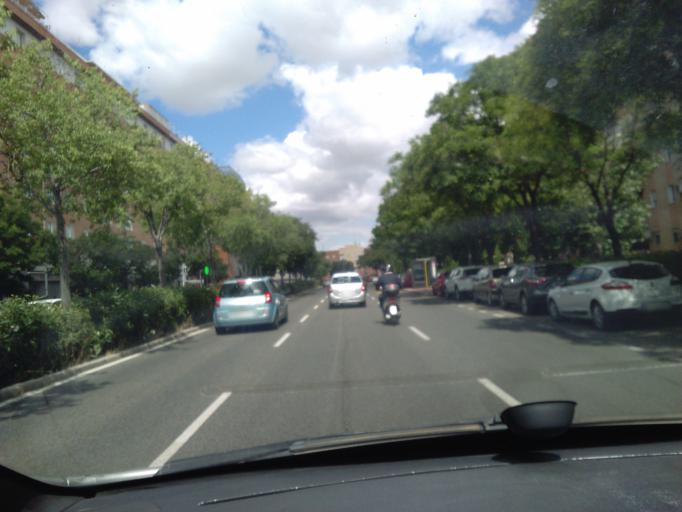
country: ES
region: Andalusia
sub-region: Provincia de Sevilla
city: Sevilla
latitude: 37.3688
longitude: -5.9803
